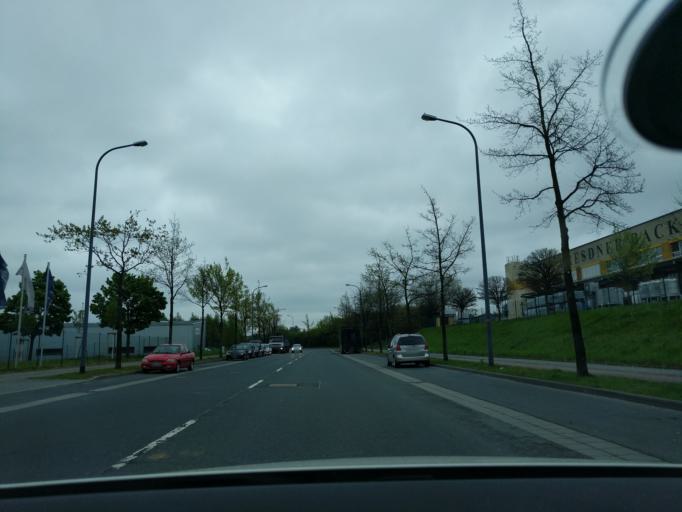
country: DE
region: Saxony
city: Bannewitz
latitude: 51.0075
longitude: 13.6954
